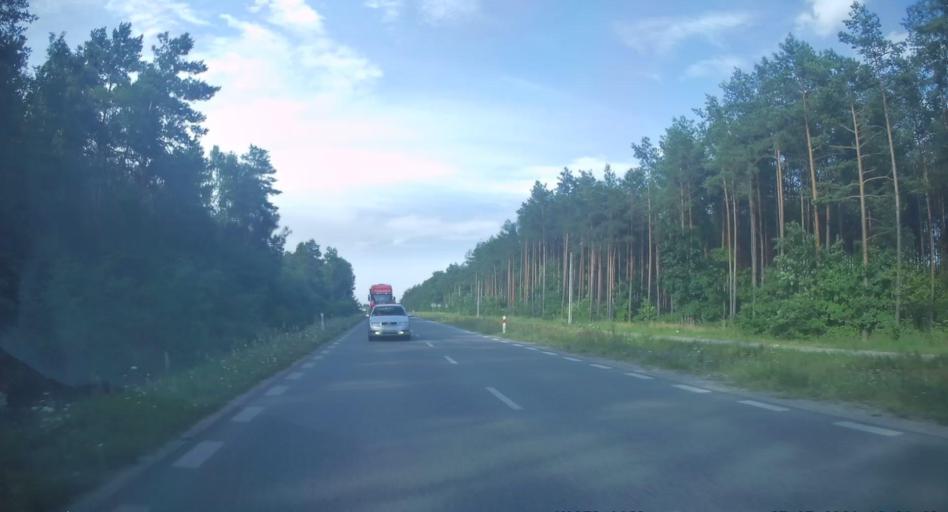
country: PL
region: Swietokrzyskie
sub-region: Powiat konecki
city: Konskie
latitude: 51.1251
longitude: 20.3572
